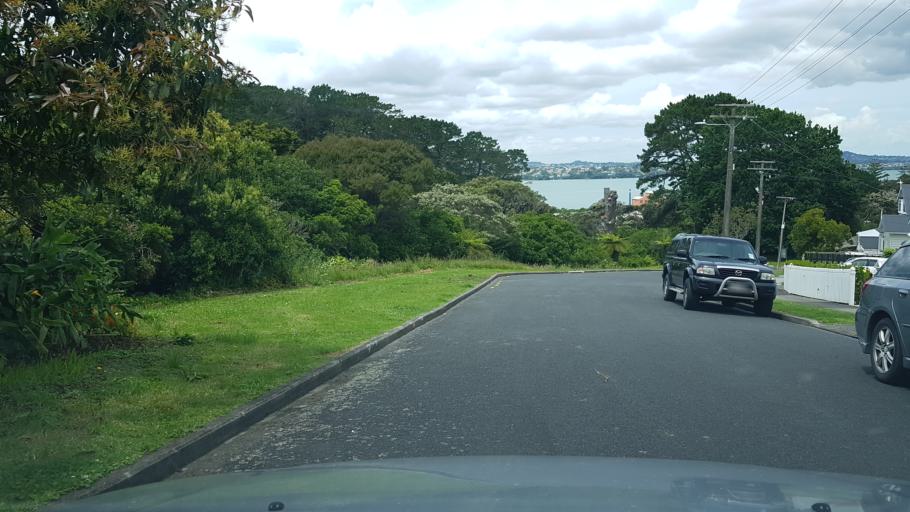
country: NZ
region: Auckland
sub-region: Auckland
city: North Shore
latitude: -36.8153
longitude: 174.7229
